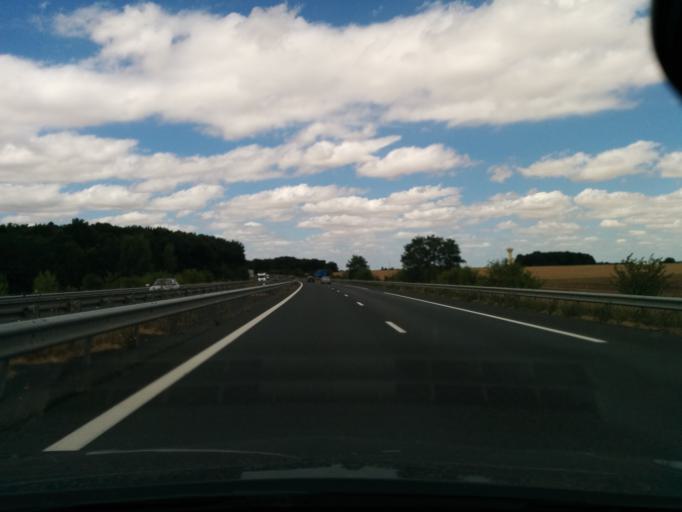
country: FR
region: Centre
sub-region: Departement de l'Indre
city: Saint-Maur
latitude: 46.7778
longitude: 1.6329
